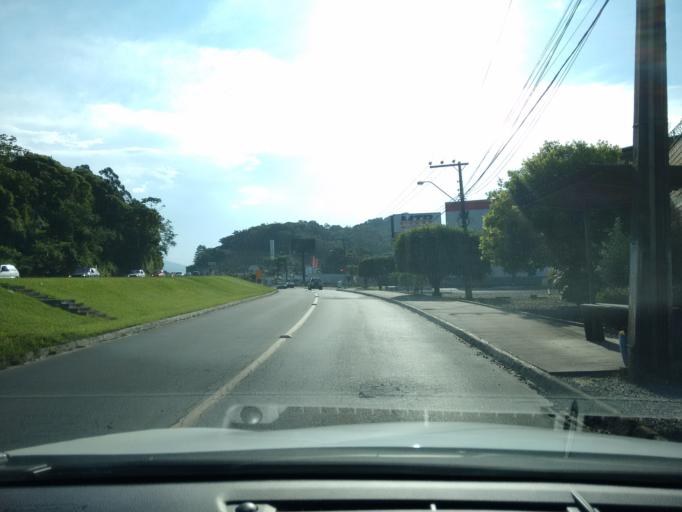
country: BR
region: Santa Catarina
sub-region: Blumenau
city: Blumenau
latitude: -26.8623
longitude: -49.0957
